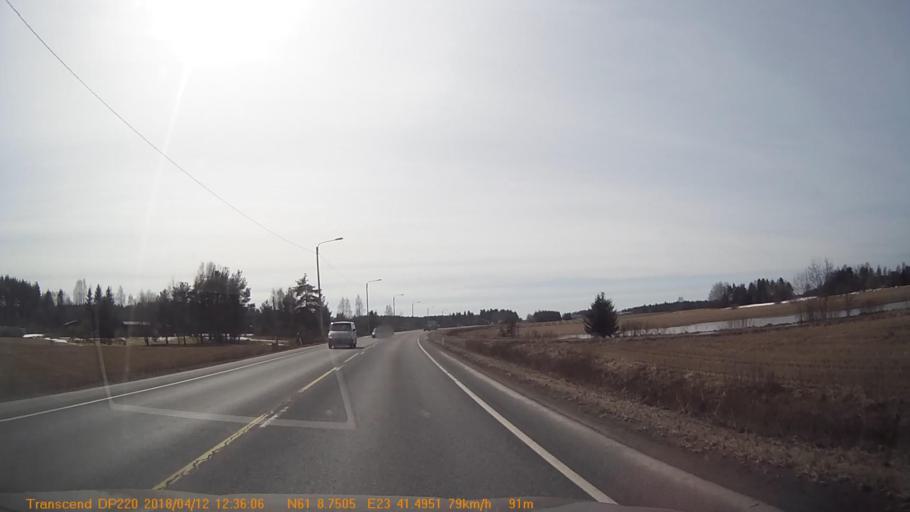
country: FI
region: Pirkanmaa
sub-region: Etelae-Pirkanmaa
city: Kylmaekoski
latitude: 61.1459
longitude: 23.6917
